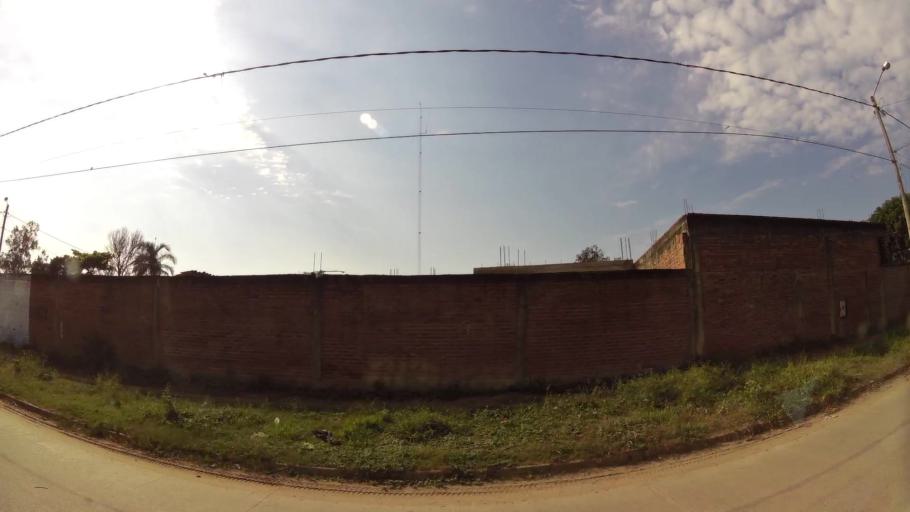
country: BO
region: Santa Cruz
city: Santa Cruz de la Sierra
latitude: -17.7308
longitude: -63.1337
